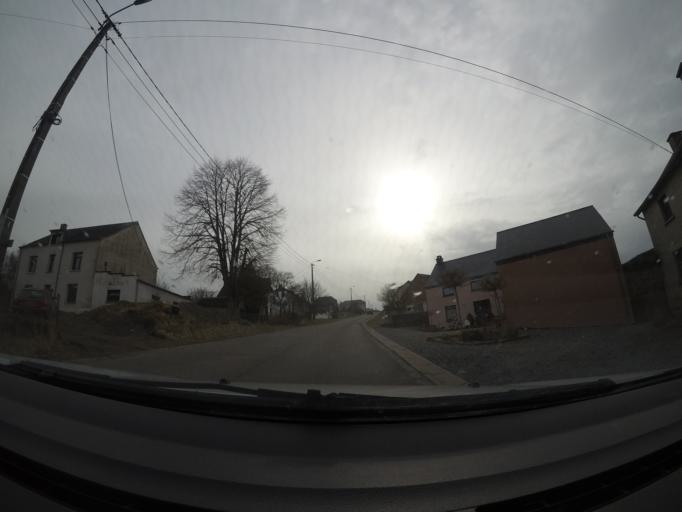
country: BE
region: Wallonia
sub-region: Province du Luxembourg
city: Martelange
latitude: 49.8284
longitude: 5.7325
